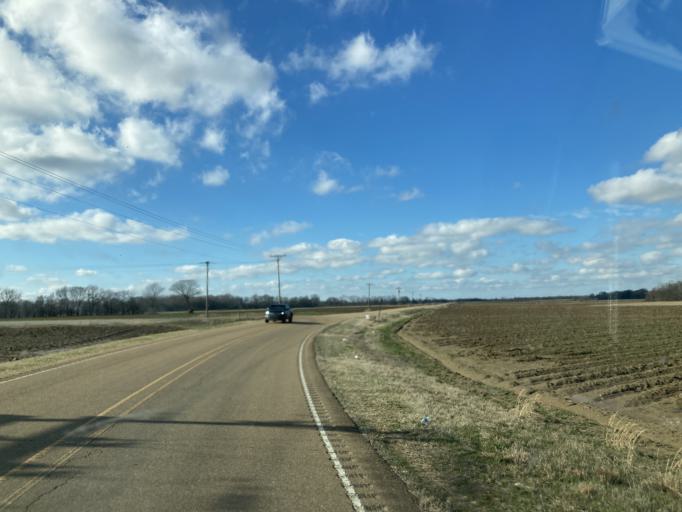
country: US
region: Mississippi
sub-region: Yazoo County
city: Yazoo City
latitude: 32.9620
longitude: -90.4930
